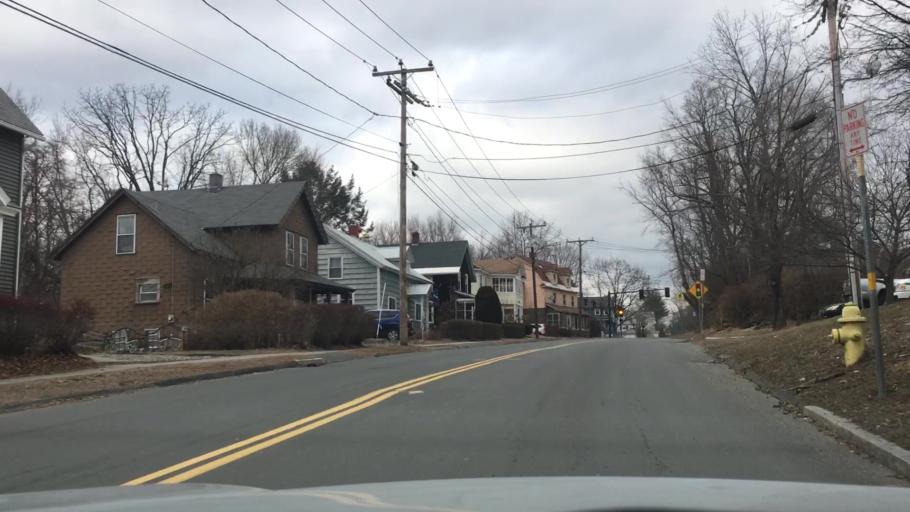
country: US
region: Massachusetts
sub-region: Franklin County
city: Greenfield
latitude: 42.5864
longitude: -72.6115
